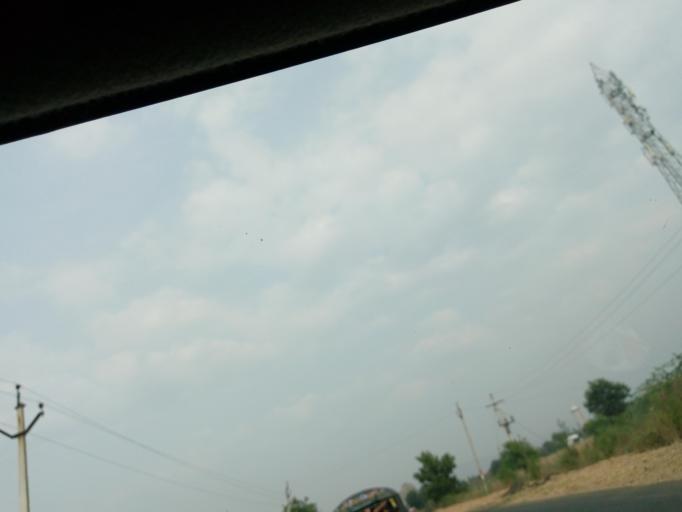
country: IN
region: Andhra Pradesh
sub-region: Prakasam
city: Diguvametta
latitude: 15.3740
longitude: 78.8754
